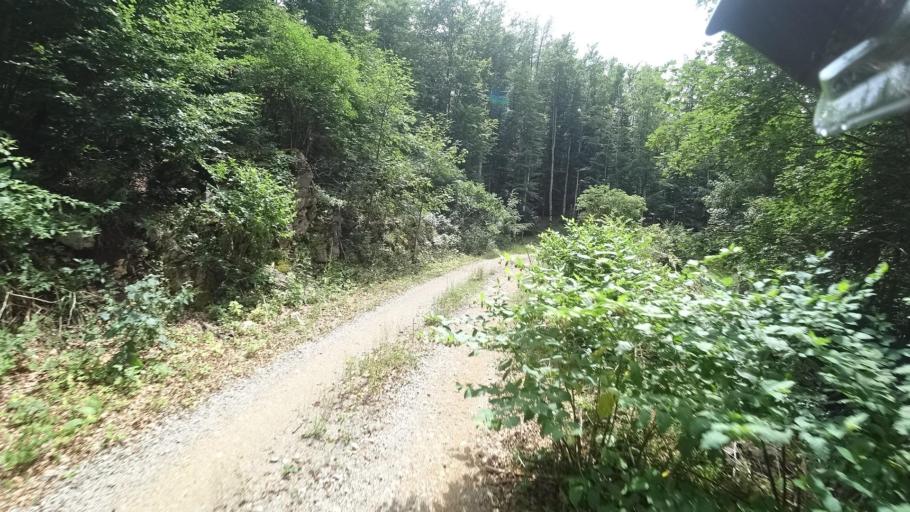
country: BA
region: Federation of Bosnia and Herzegovina
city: Bihac
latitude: 44.6389
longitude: 15.7768
